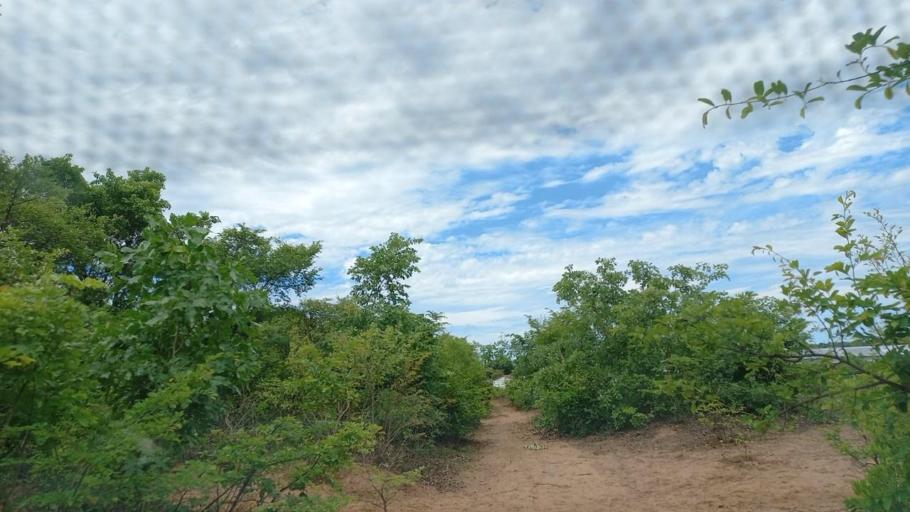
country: ZM
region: North-Western
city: Kabompo
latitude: -13.5521
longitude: 24.2715
